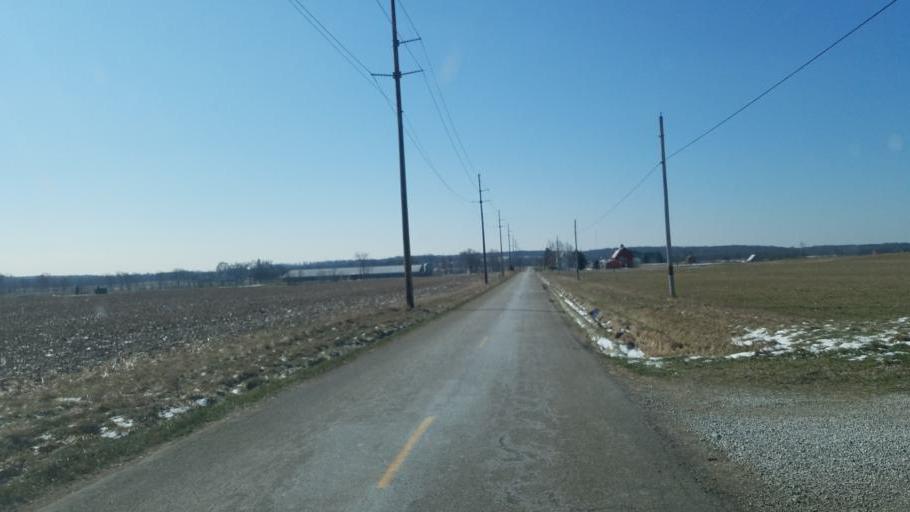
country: US
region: Ohio
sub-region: Licking County
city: Utica
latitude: 40.2781
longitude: -82.4750
